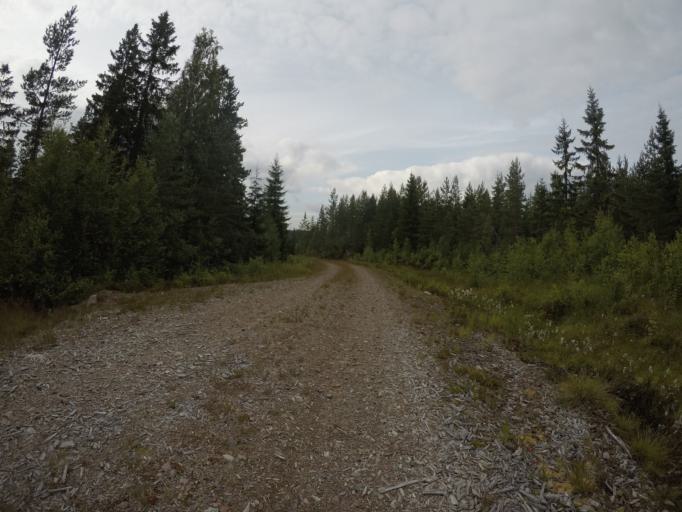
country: SE
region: Vaermland
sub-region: Filipstads Kommun
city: Lesjofors
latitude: 60.2057
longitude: 14.2630
